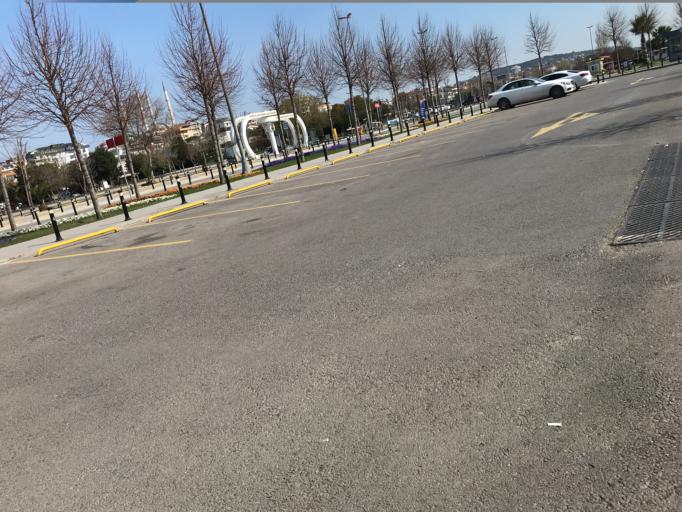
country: TR
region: Istanbul
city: Maltepe
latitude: 40.9253
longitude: 29.1228
